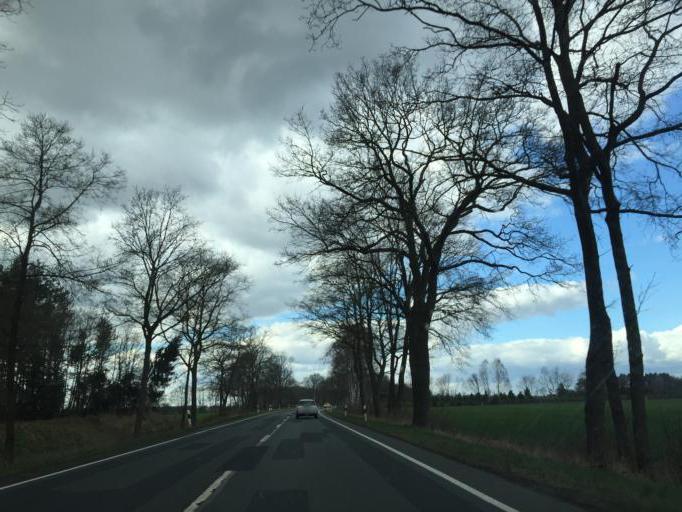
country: DE
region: Lower Saxony
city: Broeckel
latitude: 52.4924
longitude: 10.2417
